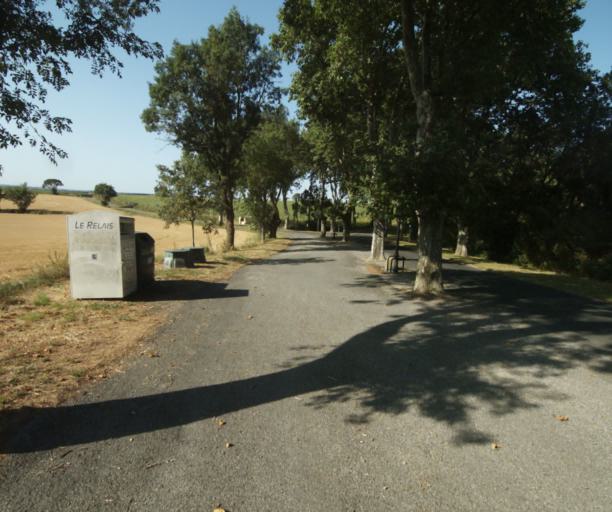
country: FR
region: Midi-Pyrenees
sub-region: Departement de la Haute-Garonne
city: Avignonet-Lauragais
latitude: 43.4267
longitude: 1.8169
